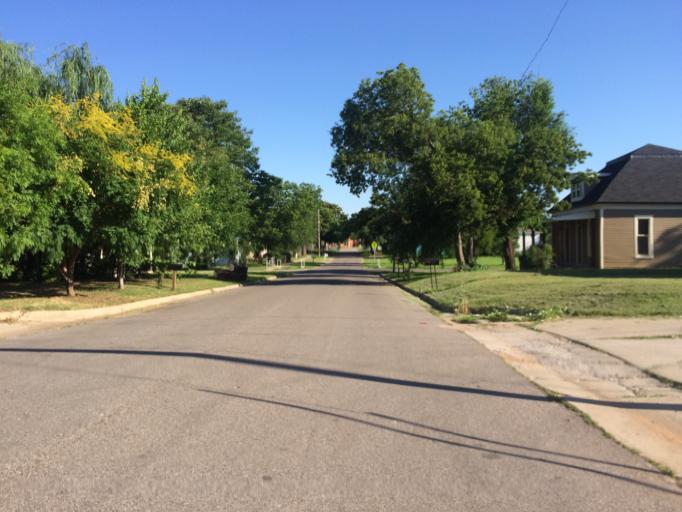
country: US
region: Oklahoma
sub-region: Cleveland County
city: Norman
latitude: 35.2235
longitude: -97.4327
